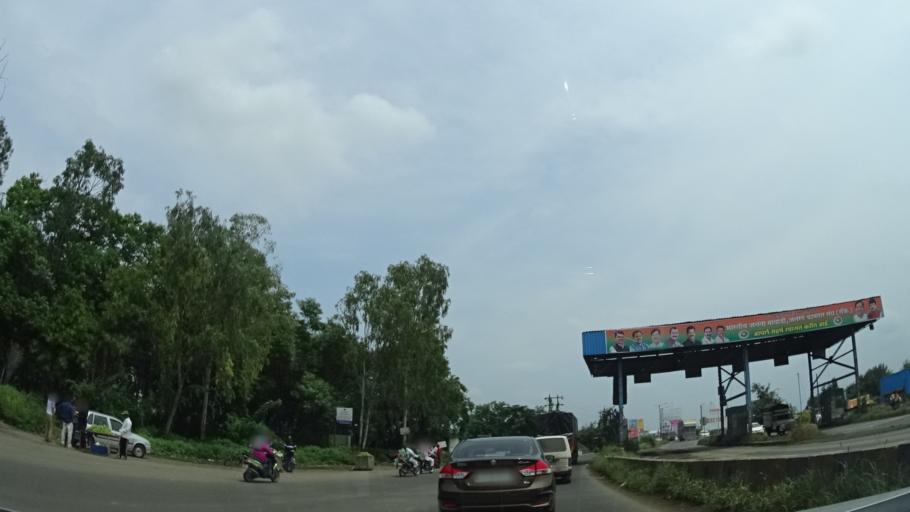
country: IN
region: Maharashtra
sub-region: Pune Division
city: Koregaon
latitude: 18.6349
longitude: 74.0438
